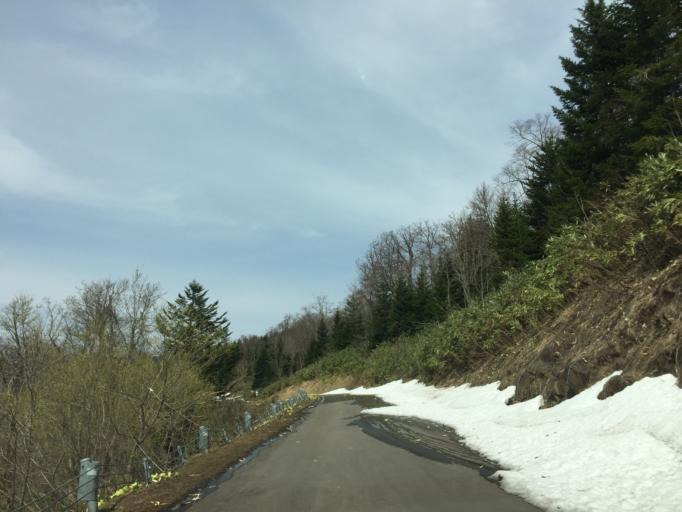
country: JP
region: Hokkaido
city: Akabira
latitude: 43.6059
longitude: 142.0677
